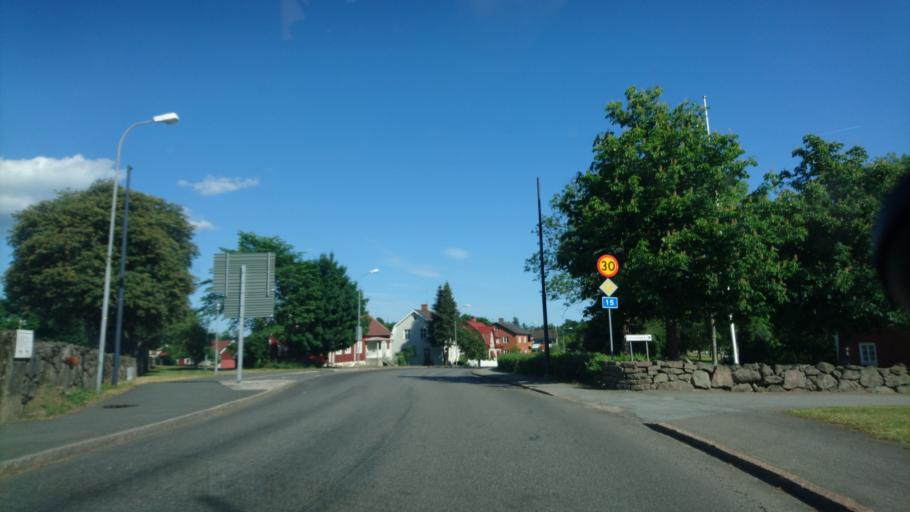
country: SE
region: Skane
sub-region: Osby Kommun
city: Lonsboda
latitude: 56.3974
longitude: 14.3233
